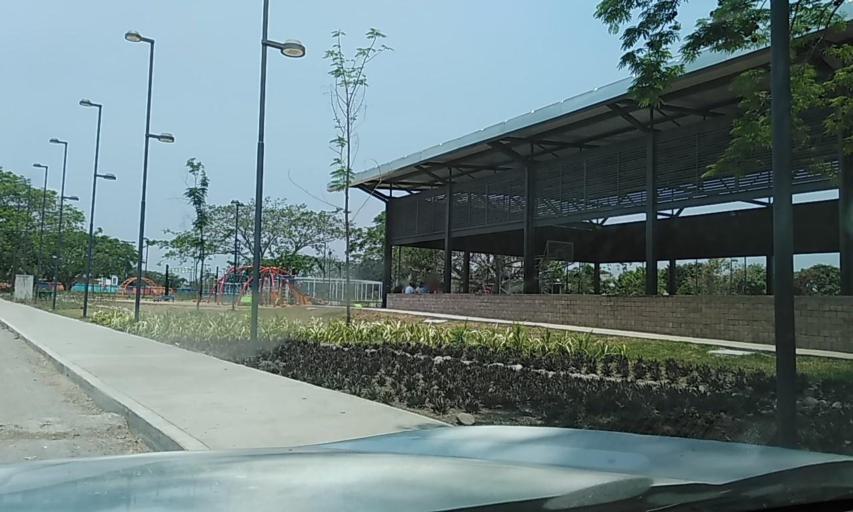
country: MX
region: Veracruz
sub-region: Veracruz
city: Las Amapolas
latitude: 19.1408
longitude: -96.1981
